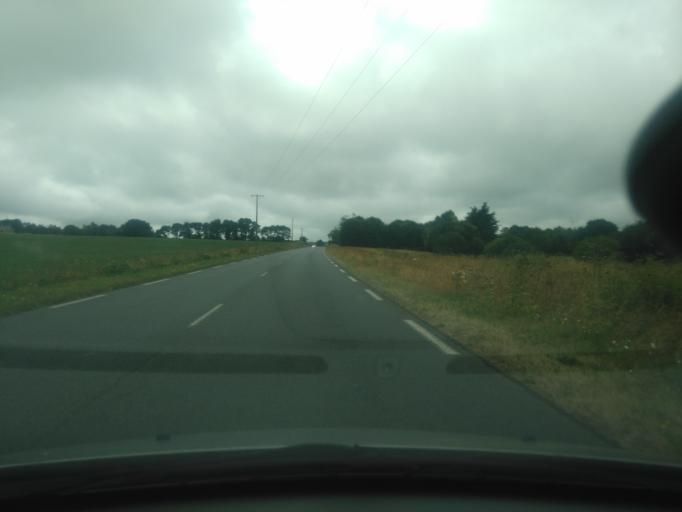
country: FR
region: Brittany
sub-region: Departement des Cotes-d'Armor
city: Quintin
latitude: 48.3726
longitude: -2.9411
